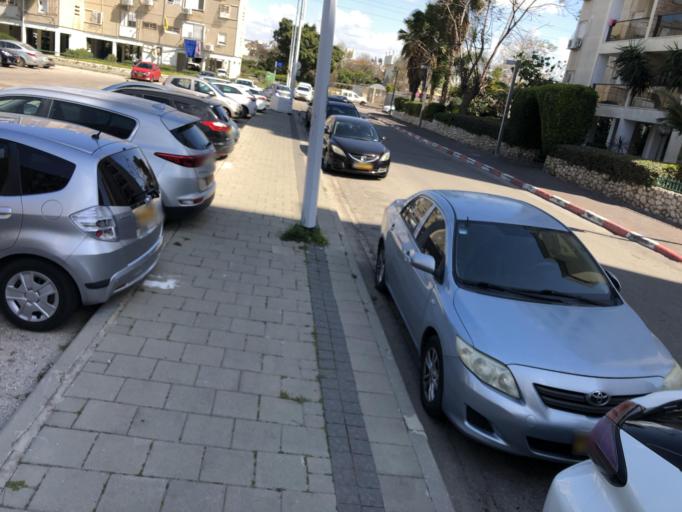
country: IL
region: Tel Aviv
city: Bat Yam
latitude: 32.0078
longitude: 34.7592
